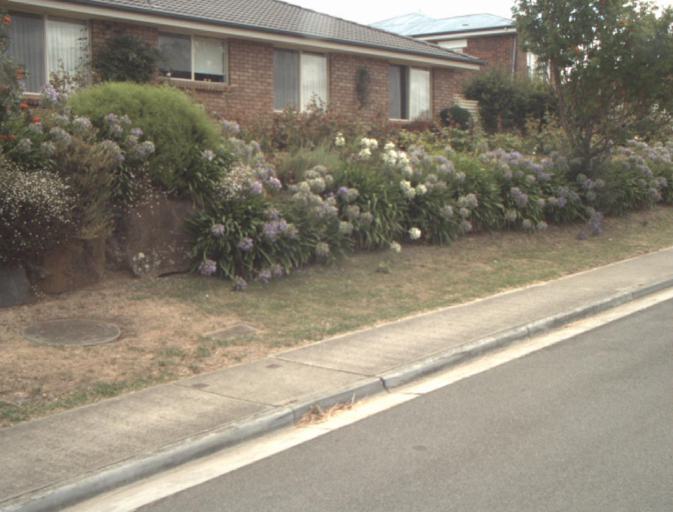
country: AU
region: Tasmania
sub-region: Launceston
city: Newstead
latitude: -41.4611
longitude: 147.1825
